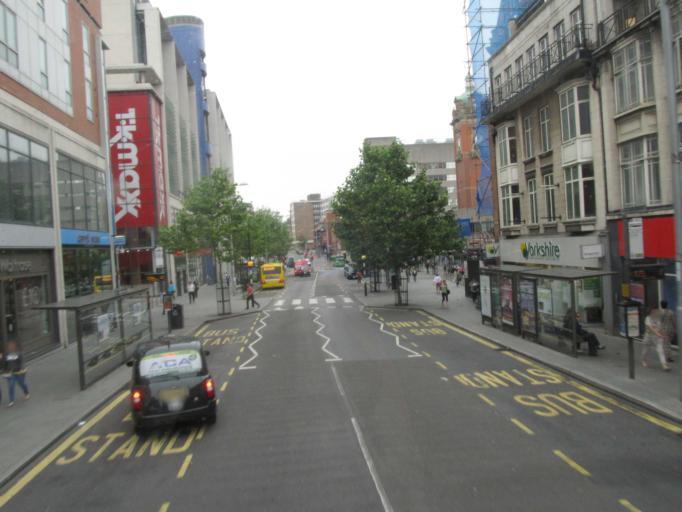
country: GB
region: England
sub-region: Nottingham
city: Nottingham
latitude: 52.9560
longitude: -1.1481
